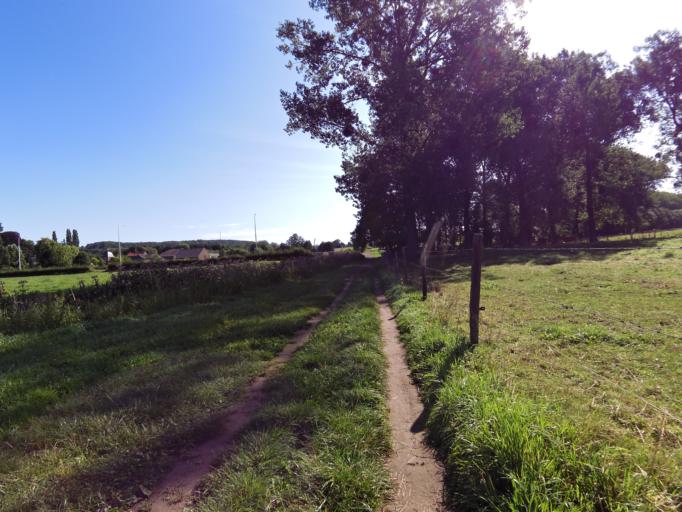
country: NL
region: Limburg
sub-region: Valkenburg aan de Geul
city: Schin op Geul
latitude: 50.8202
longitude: 5.8998
